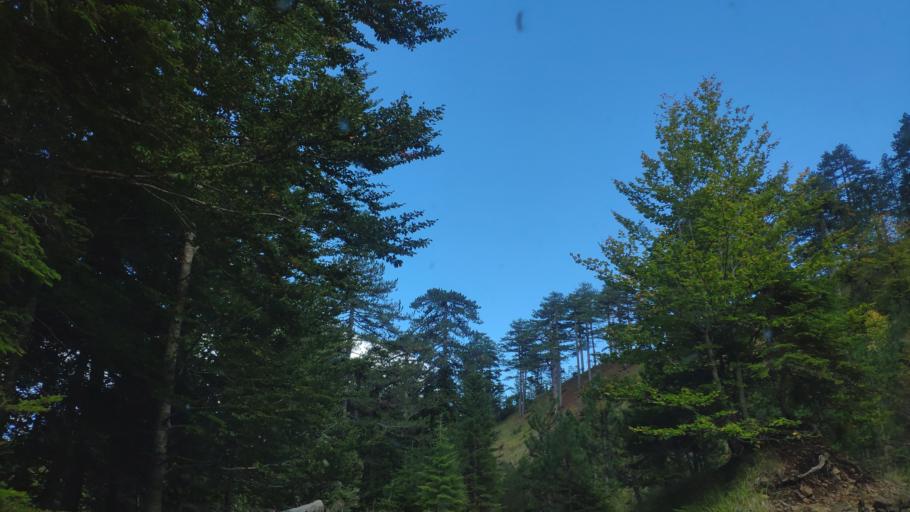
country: AL
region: Korce
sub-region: Rrethi i Devollit
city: Miras
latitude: 40.3371
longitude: 20.8981
